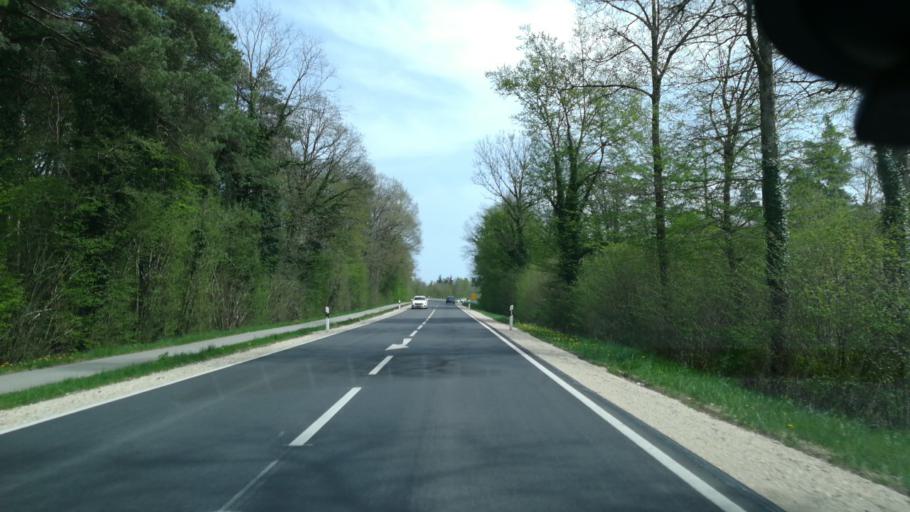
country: DE
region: Baden-Wuerttemberg
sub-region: Freiburg Region
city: Moos
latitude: 47.7596
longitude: 8.9006
